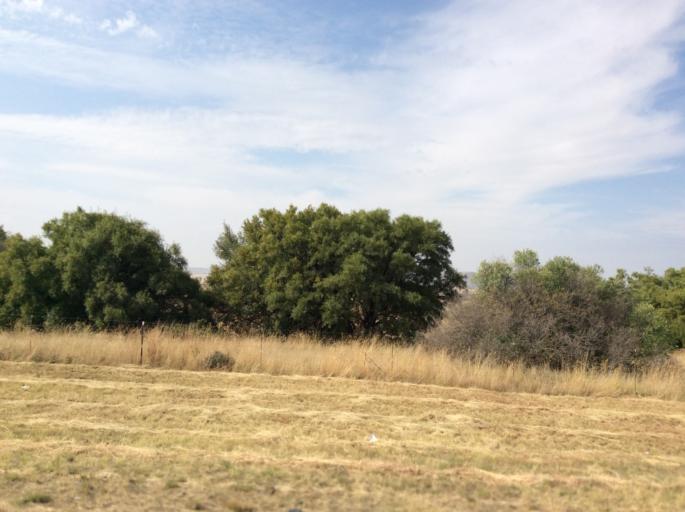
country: ZA
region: Orange Free State
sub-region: Xhariep District Municipality
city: Dewetsdorp
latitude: -29.5658
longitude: 26.6660
